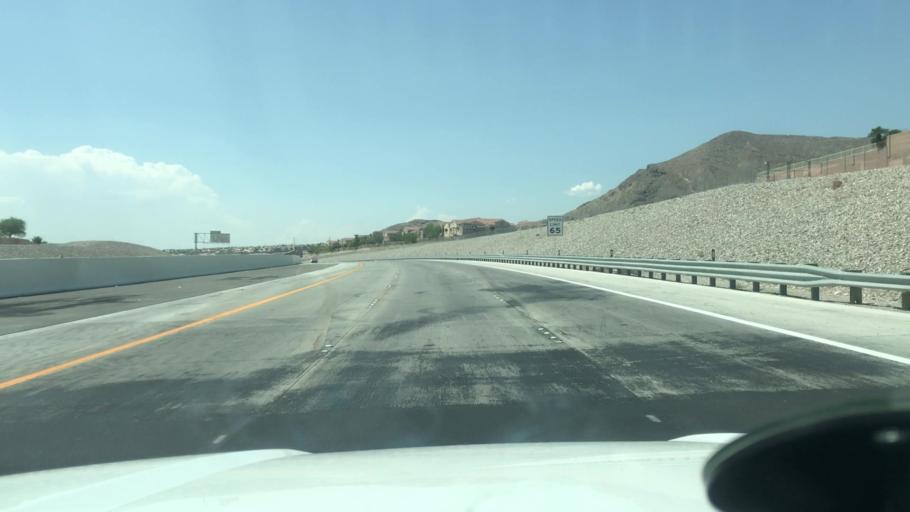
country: US
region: Nevada
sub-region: Clark County
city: Summerlin South
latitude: 36.2392
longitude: -115.3249
